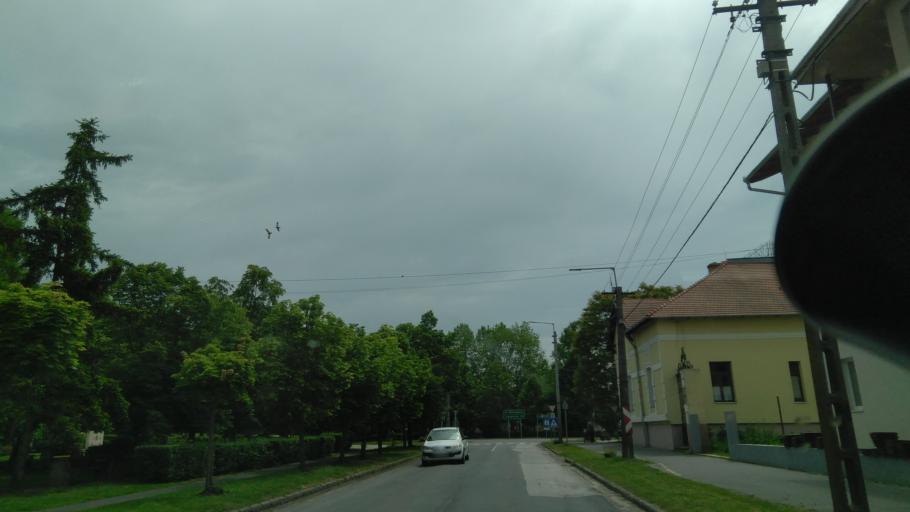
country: HU
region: Bekes
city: Fuzesgyarmat
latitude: 47.1084
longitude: 21.2118
